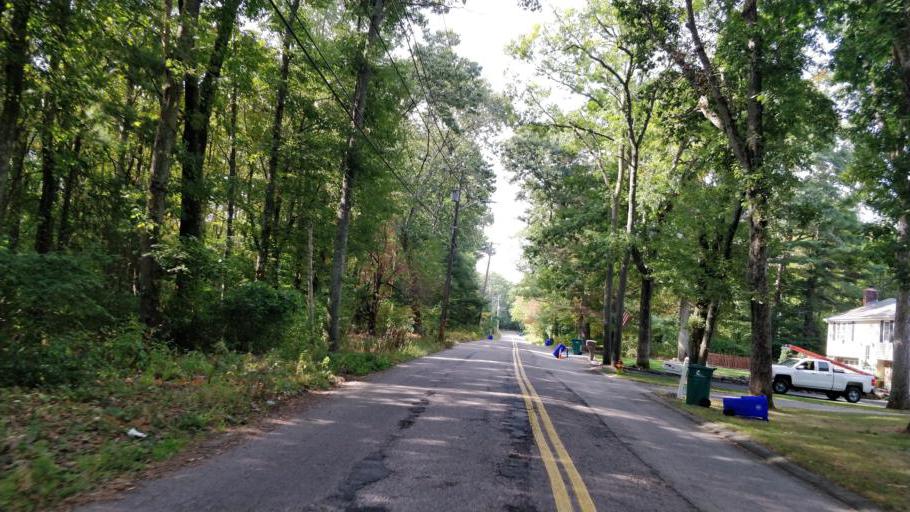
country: US
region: Massachusetts
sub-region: Bristol County
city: Attleboro
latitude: 41.9399
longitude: -71.2426
